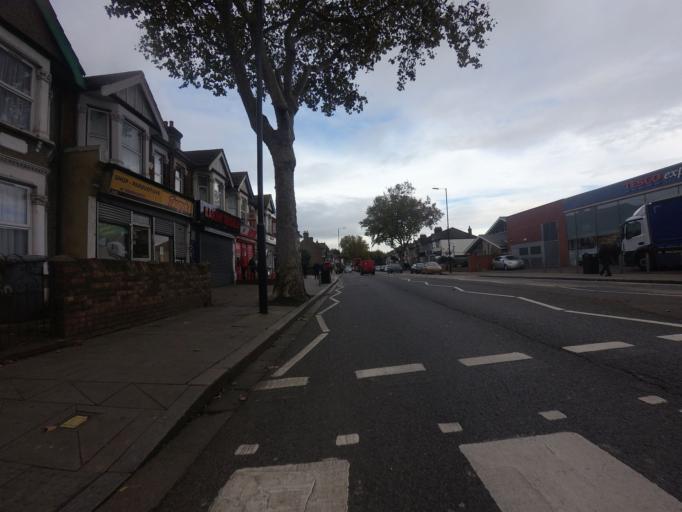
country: GB
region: England
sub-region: Greater London
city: East Ham
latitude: 51.5258
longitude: 0.0567
